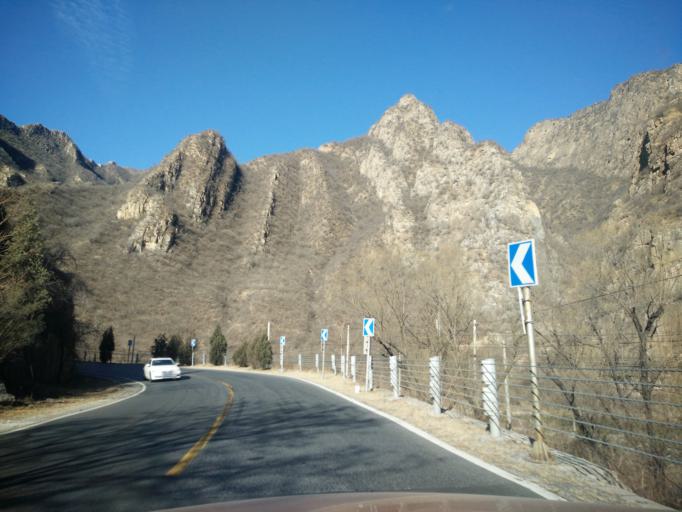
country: CN
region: Beijing
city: Yanchi
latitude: 40.0111
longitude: 115.7922
